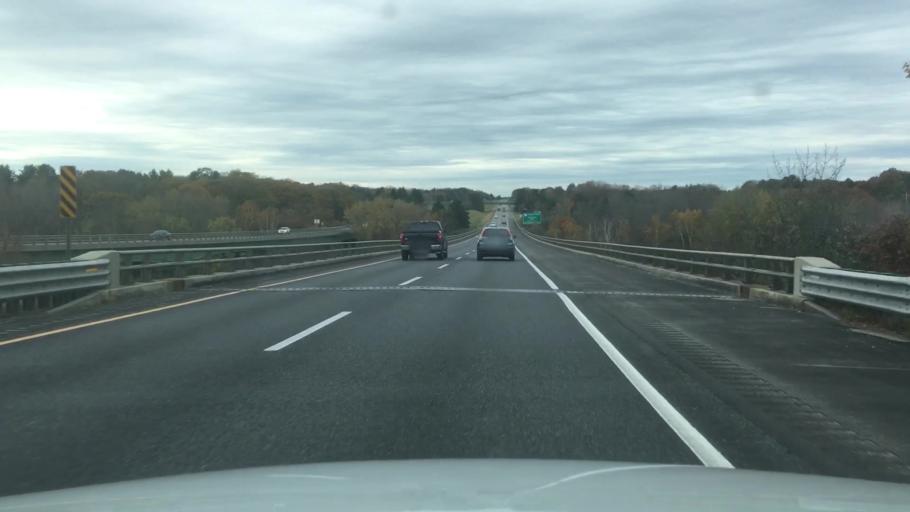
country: US
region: Maine
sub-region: Sagadahoc County
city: Topsham
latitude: 43.9322
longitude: -69.9926
